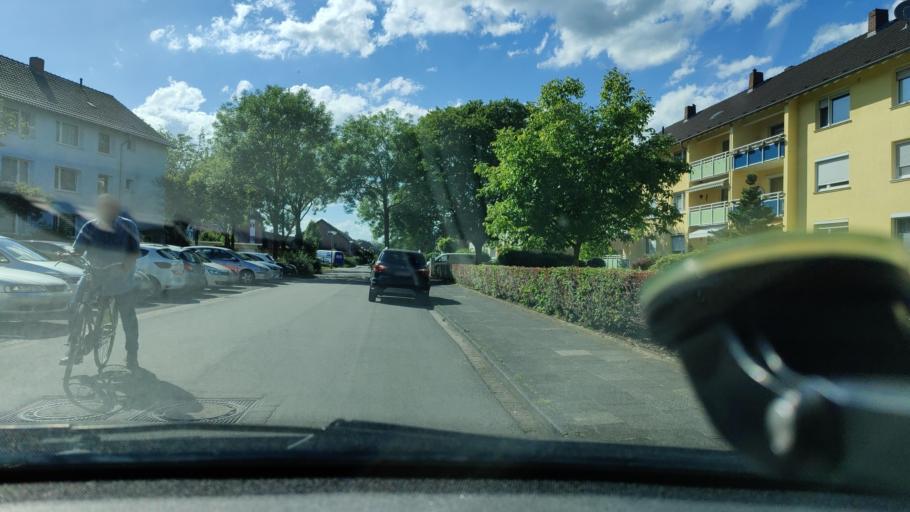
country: DE
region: North Rhine-Westphalia
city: Rheinberg
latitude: 51.5502
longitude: 6.5887
